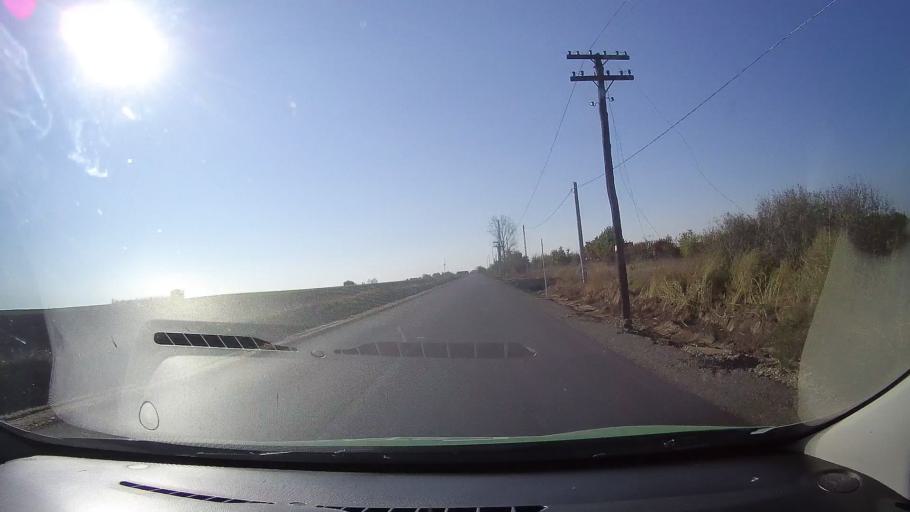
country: RO
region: Satu Mare
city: Carei
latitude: 47.6627
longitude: 22.4605
